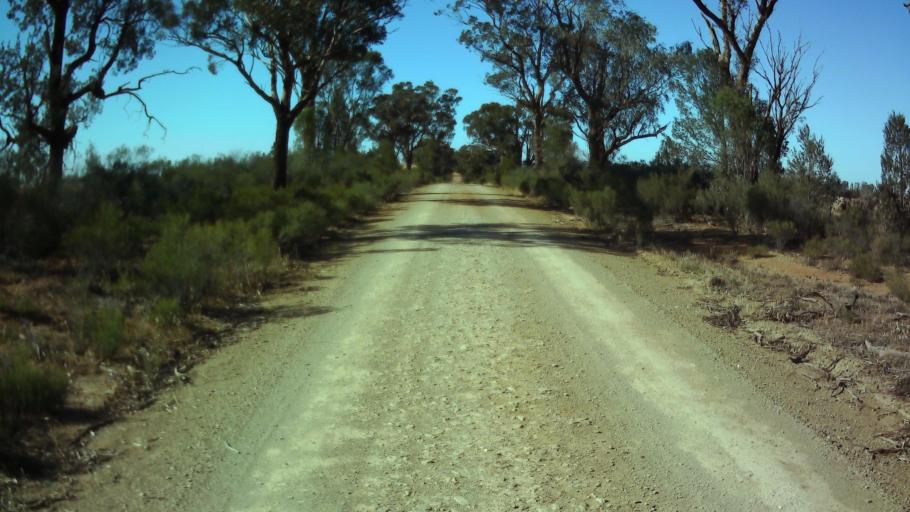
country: AU
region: New South Wales
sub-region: Weddin
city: Grenfell
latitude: -33.8897
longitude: 147.8807
